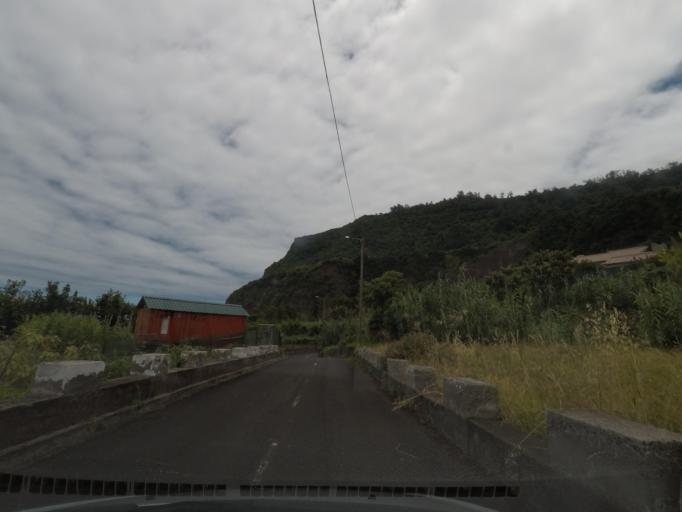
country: PT
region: Madeira
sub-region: Santana
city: Santana
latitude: 32.8273
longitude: -16.9509
